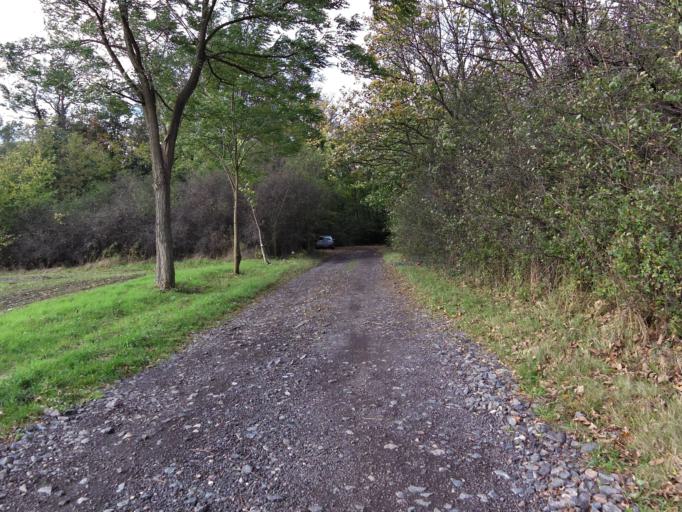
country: DE
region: Saxony
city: Grossposna
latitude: 51.2893
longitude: 12.4898
